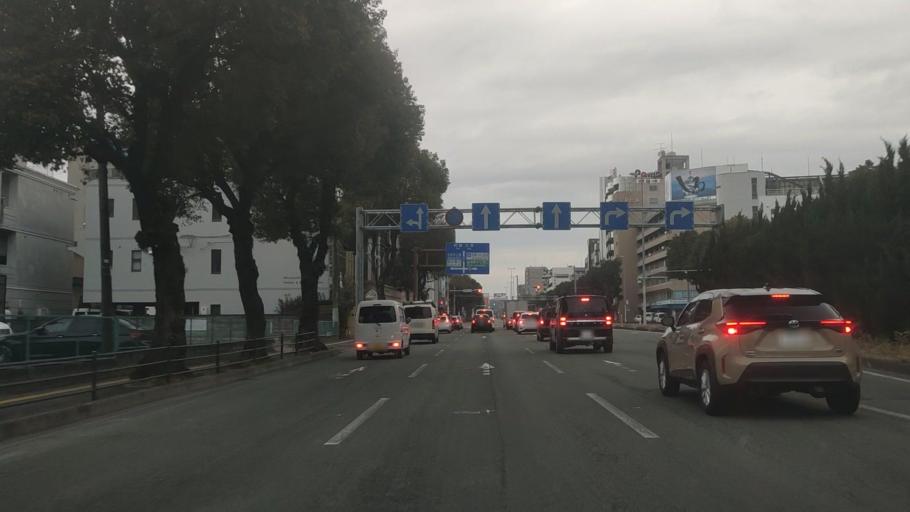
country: JP
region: Kumamoto
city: Kumamoto
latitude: 32.7867
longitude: 130.7465
